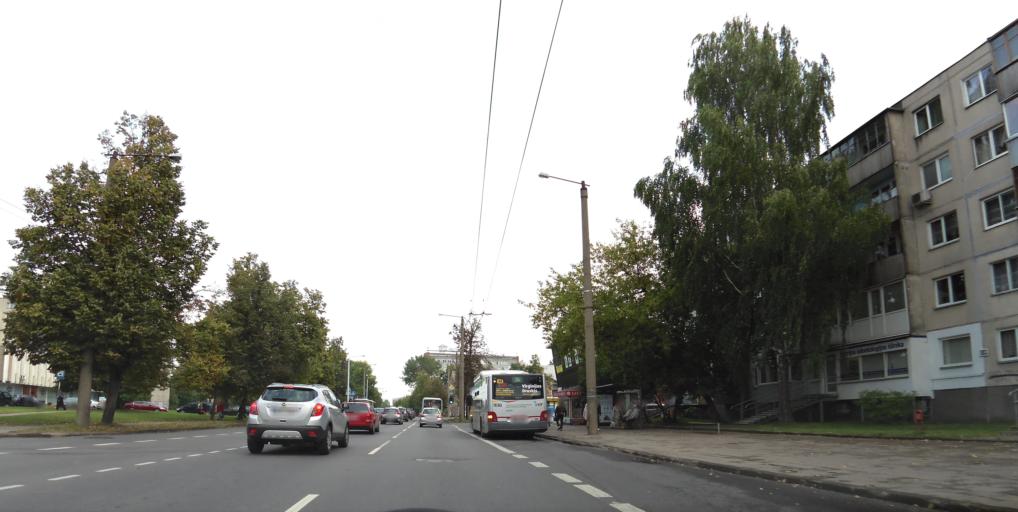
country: LT
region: Vilnius County
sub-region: Vilnius
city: Vilnius
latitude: 54.7077
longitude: 25.2853
